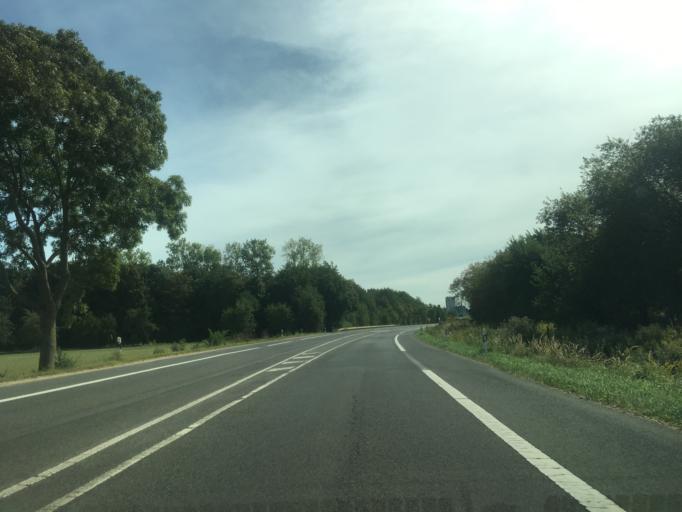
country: DE
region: North Rhine-Westphalia
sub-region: Regierungsbezirk Koln
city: Titz
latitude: 51.0522
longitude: 6.3878
